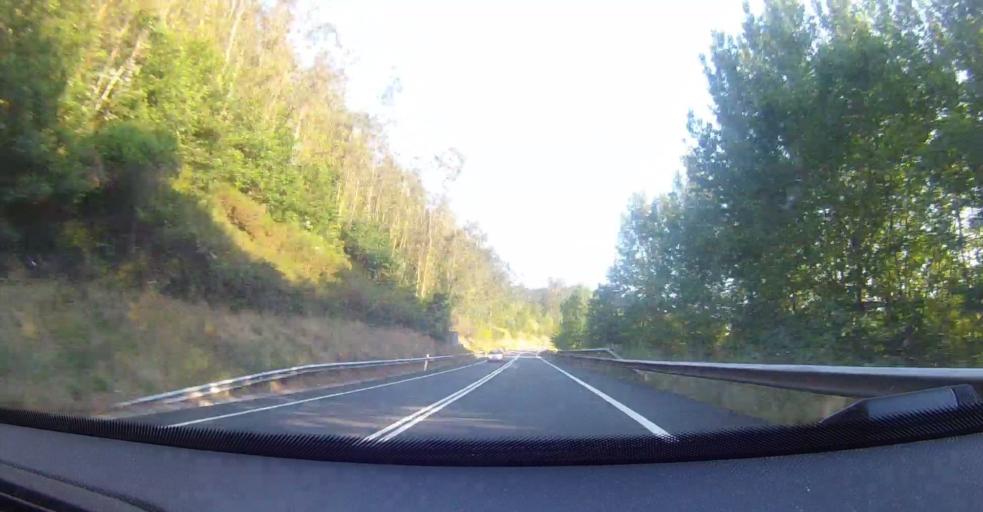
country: ES
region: Cantabria
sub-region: Provincia de Cantabria
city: Ampuero
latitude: 43.3384
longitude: -3.4076
